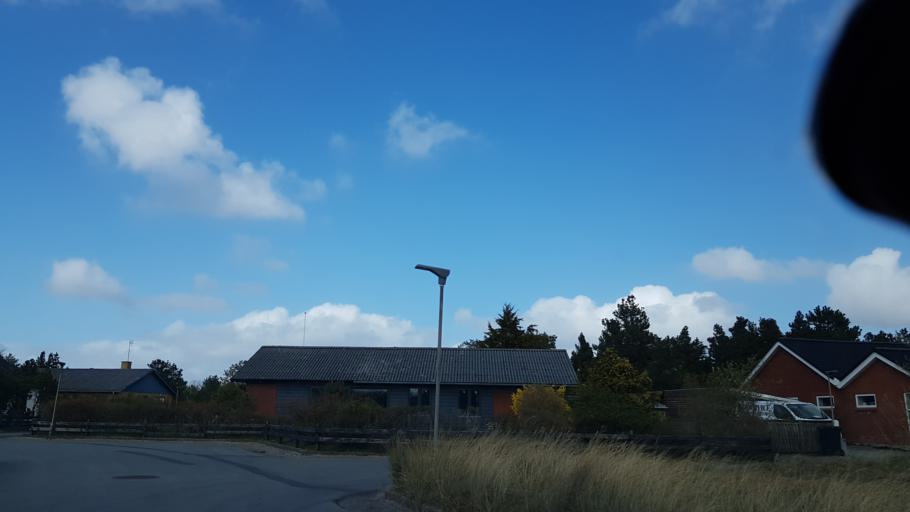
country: DE
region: Schleswig-Holstein
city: List
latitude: 55.0882
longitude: 8.5539
